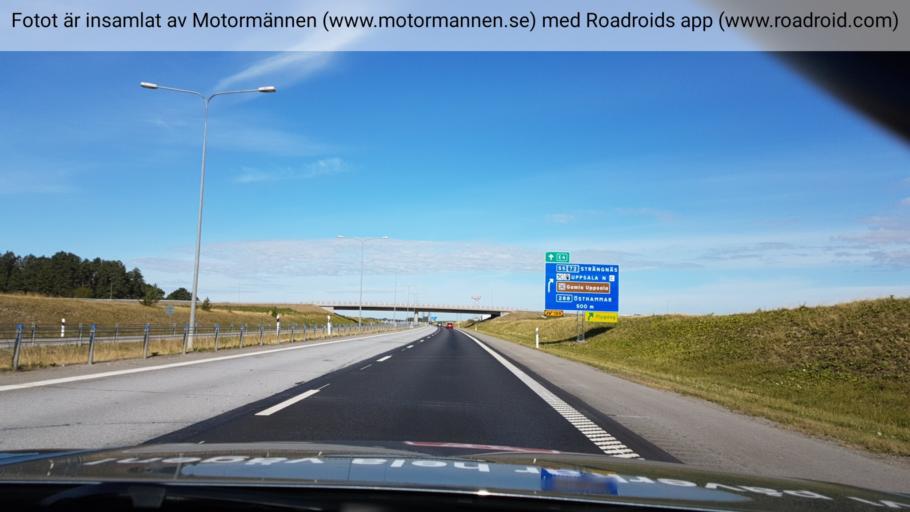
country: SE
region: Uppsala
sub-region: Uppsala Kommun
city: Uppsala
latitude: 59.8797
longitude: 17.6911
